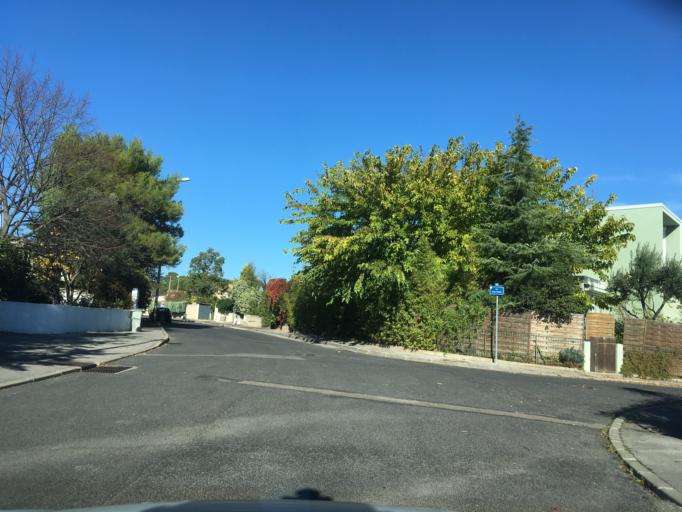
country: FR
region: Languedoc-Roussillon
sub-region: Departement de l'Herault
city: Juvignac
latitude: 43.6030
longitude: 3.8350
